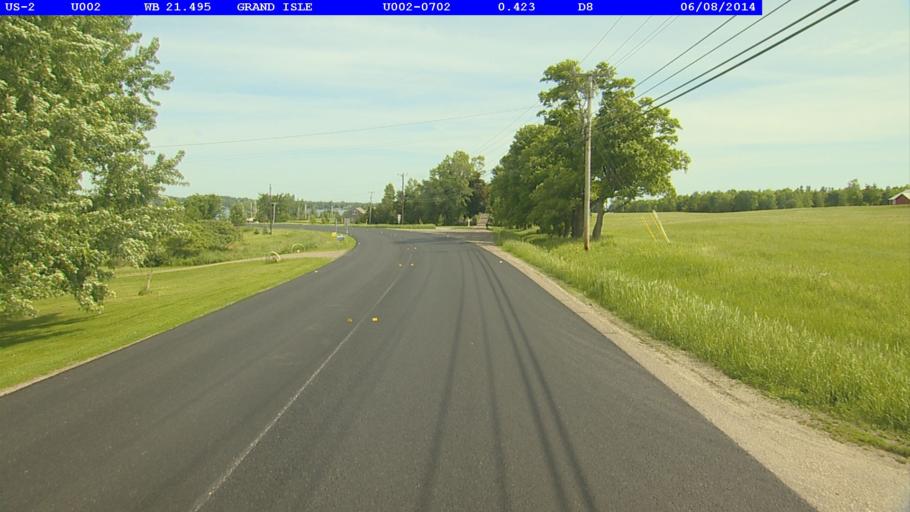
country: US
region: Vermont
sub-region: Grand Isle County
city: North Hero
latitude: 44.7612
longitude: -73.2855
